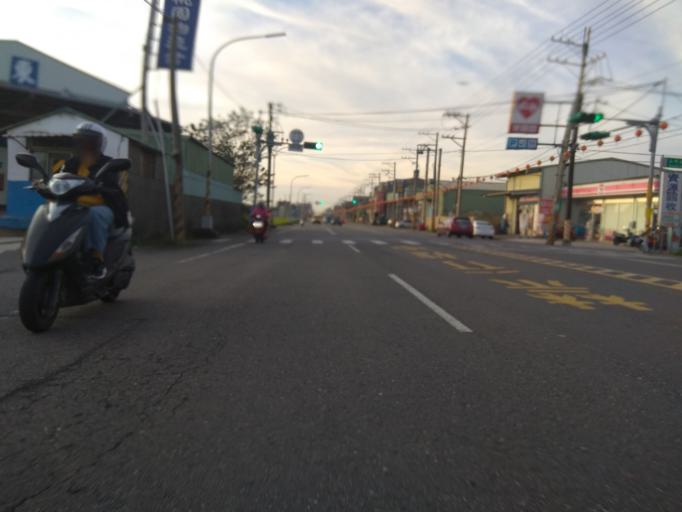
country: TW
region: Taiwan
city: Taoyuan City
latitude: 25.0018
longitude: 121.1545
